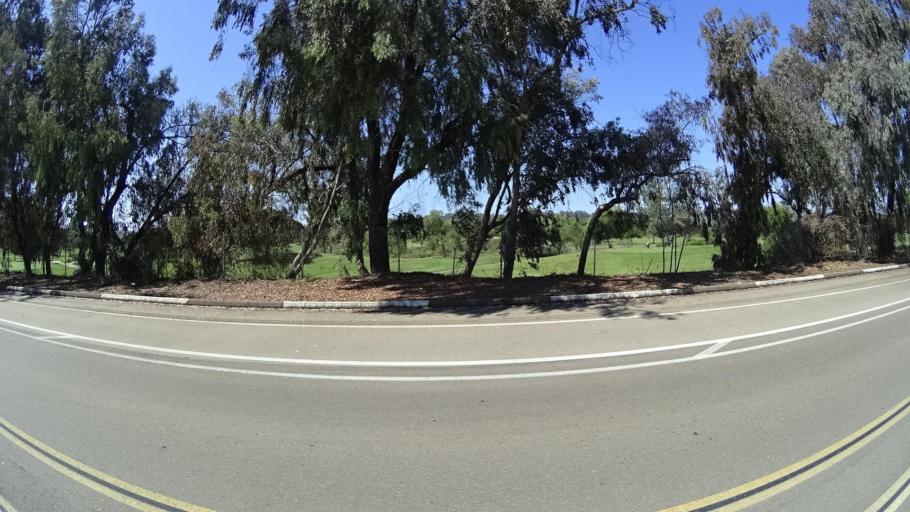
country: US
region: California
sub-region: San Diego County
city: Fairbanks Ranch
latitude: 32.9826
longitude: -117.2055
